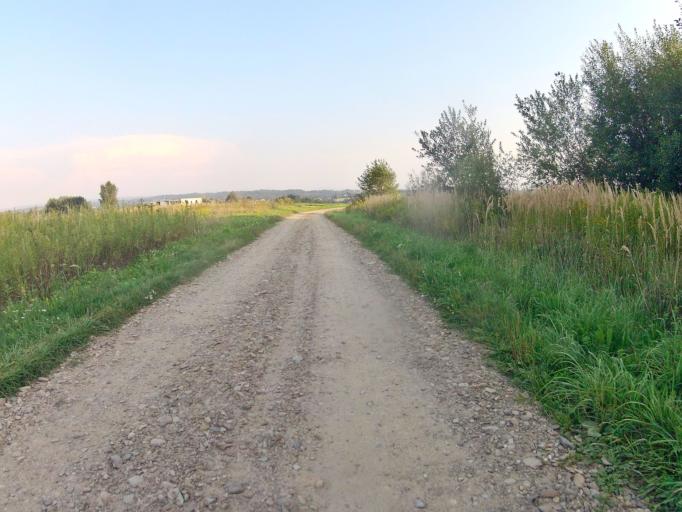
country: PL
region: Subcarpathian Voivodeship
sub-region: Powiat jasielski
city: Brzyska
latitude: 49.7873
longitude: 21.3872
